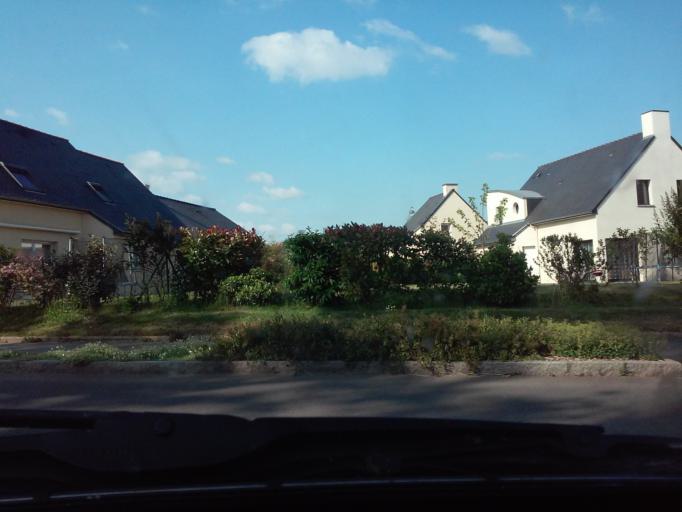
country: FR
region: Brittany
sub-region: Departement d'Ille-et-Vilaine
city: Liffre
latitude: 48.2055
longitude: -1.5203
